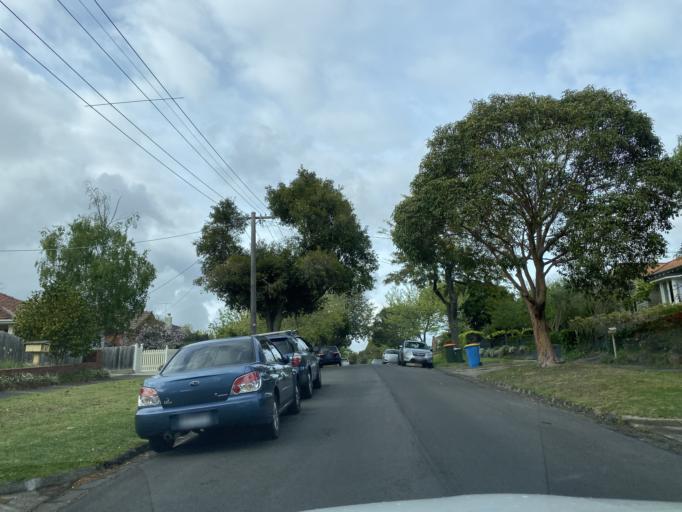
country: AU
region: Victoria
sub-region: Boroondara
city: Canterbury
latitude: -37.8325
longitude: 145.0902
